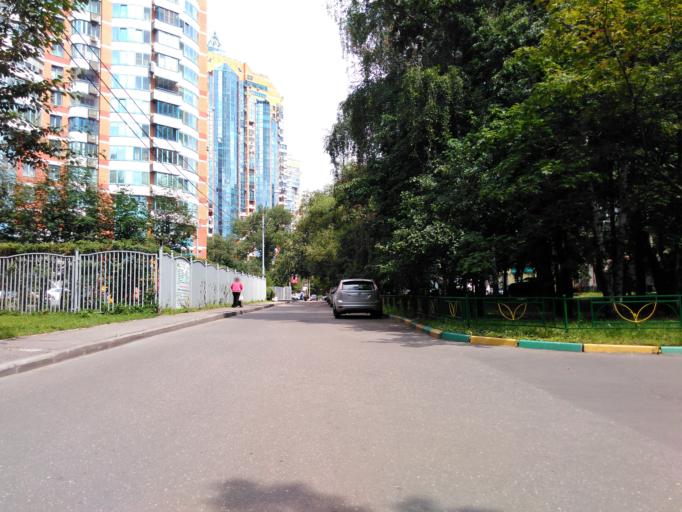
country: RU
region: Moscow
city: Troparevo
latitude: 55.6660
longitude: 37.5102
